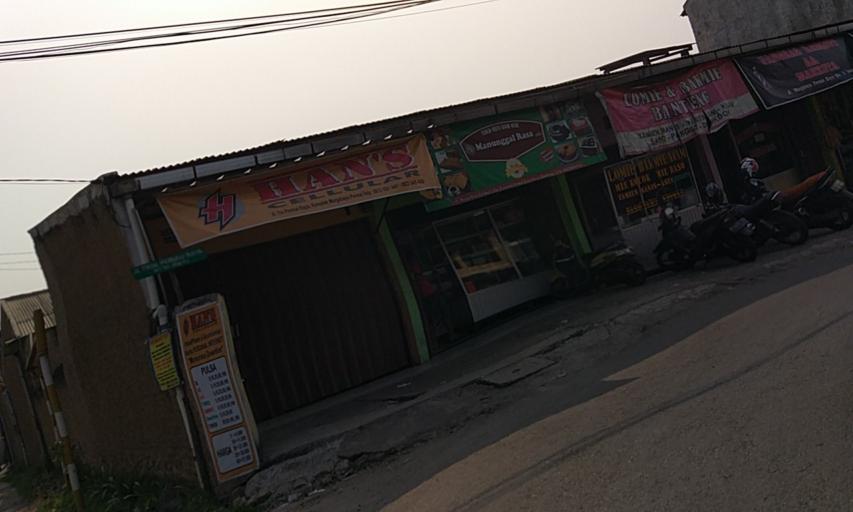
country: ID
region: West Java
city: Margahayukencana
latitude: -6.9732
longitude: 107.5564
